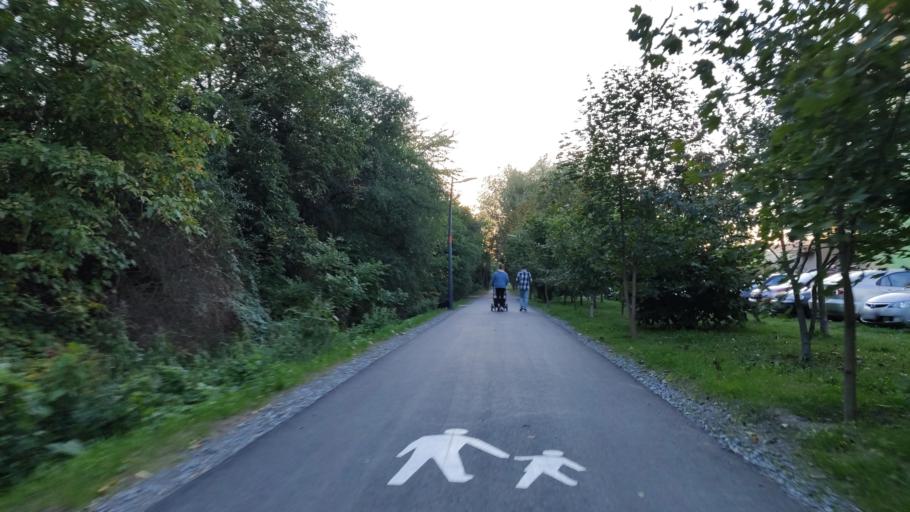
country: PL
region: Lower Silesian Voivodeship
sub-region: Powiat wroclawski
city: Wroclaw
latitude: 51.0713
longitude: 17.0473
